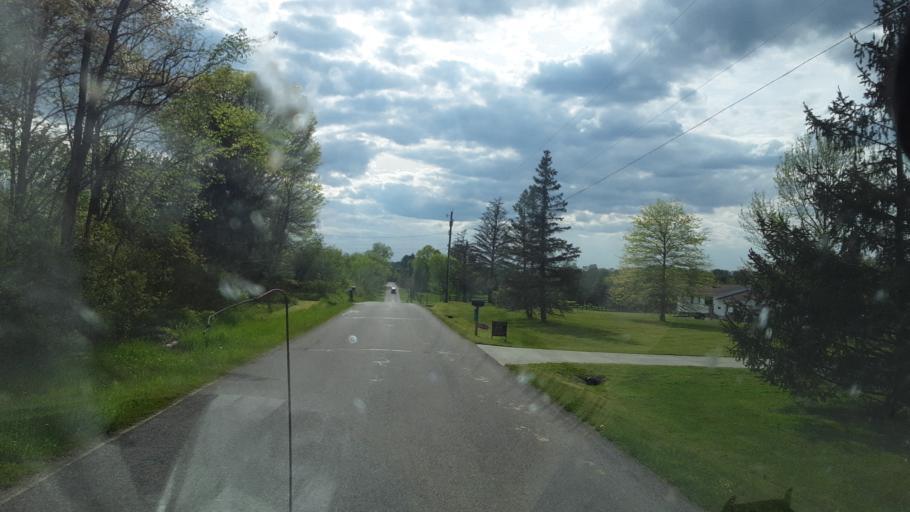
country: US
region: Ohio
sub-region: Portage County
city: Garrettsville
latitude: 41.3478
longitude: -81.0142
